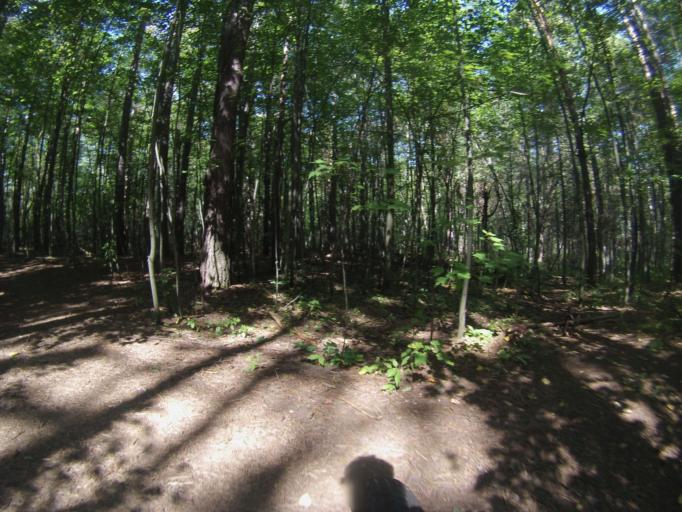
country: CA
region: Ontario
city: Ottawa
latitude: 45.3565
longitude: -75.6172
